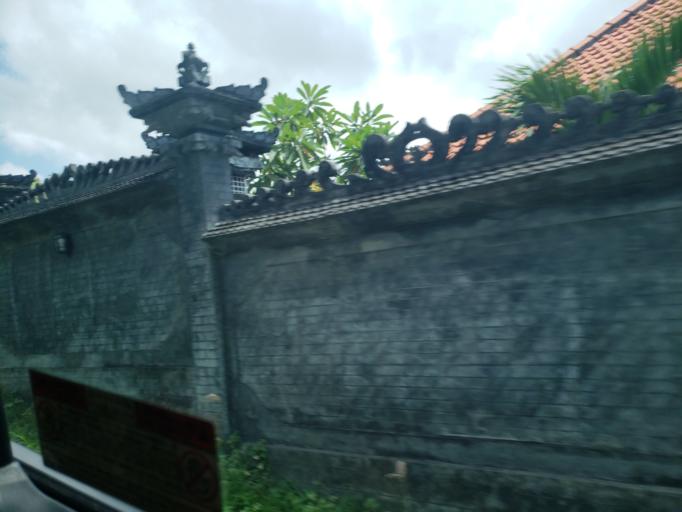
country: ID
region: Bali
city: Kangin
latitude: -8.8441
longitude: 115.1470
